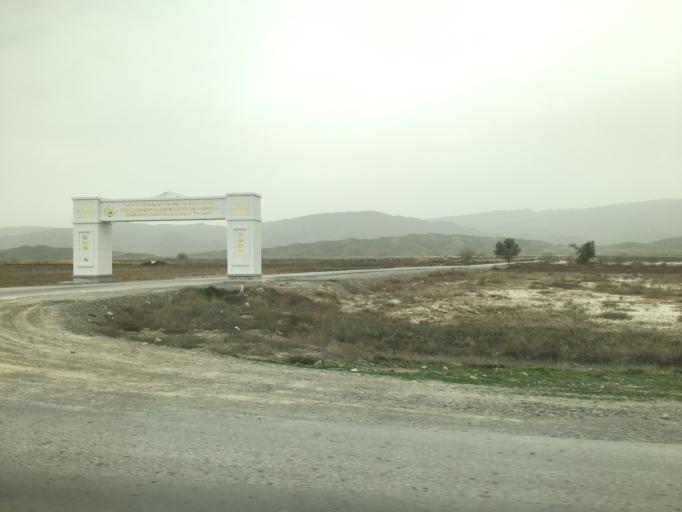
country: TM
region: Ahal
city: Baharly
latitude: 38.3495
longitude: 57.5501
